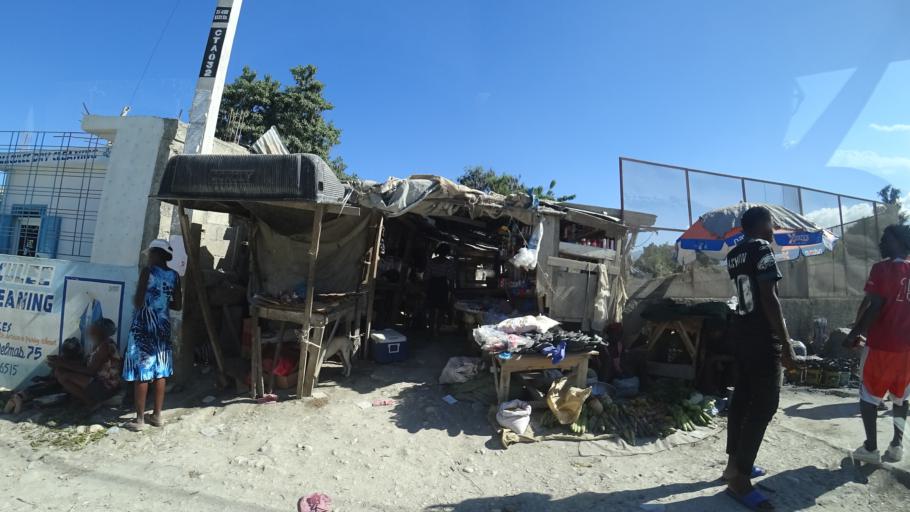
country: HT
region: Ouest
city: Delmas 73
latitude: 18.5534
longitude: -72.2851
